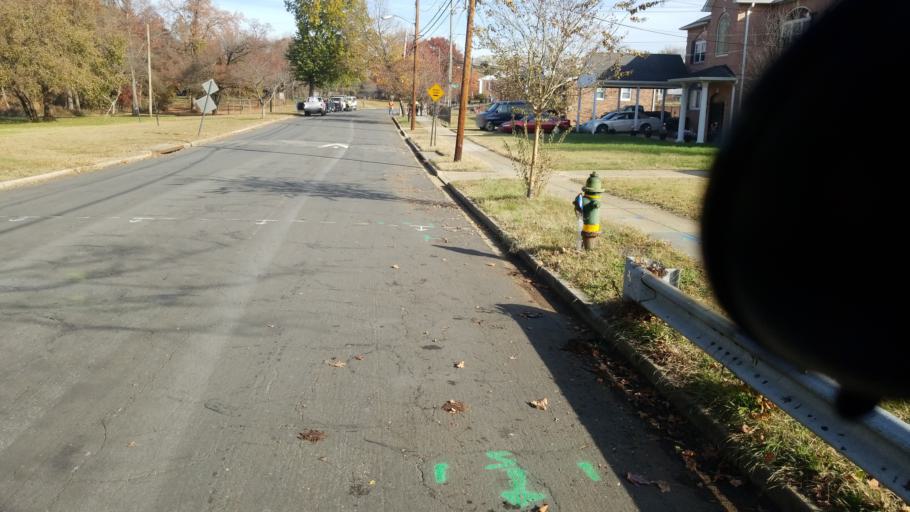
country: US
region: Maryland
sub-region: Prince George's County
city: Colmar Manor
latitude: 38.9106
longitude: -76.9418
